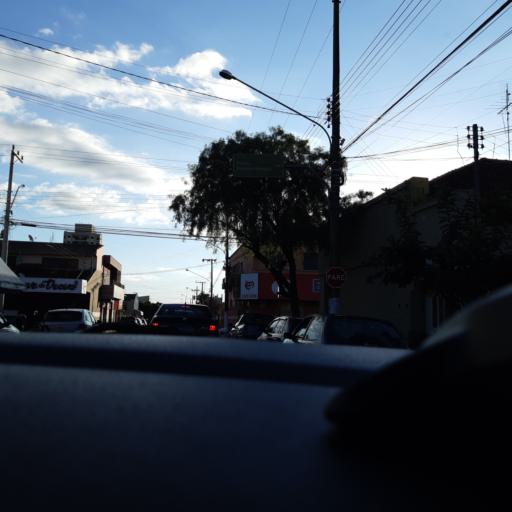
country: BR
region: Sao Paulo
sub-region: Ourinhos
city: Ourinhos
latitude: -22.9828
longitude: -49.8659
